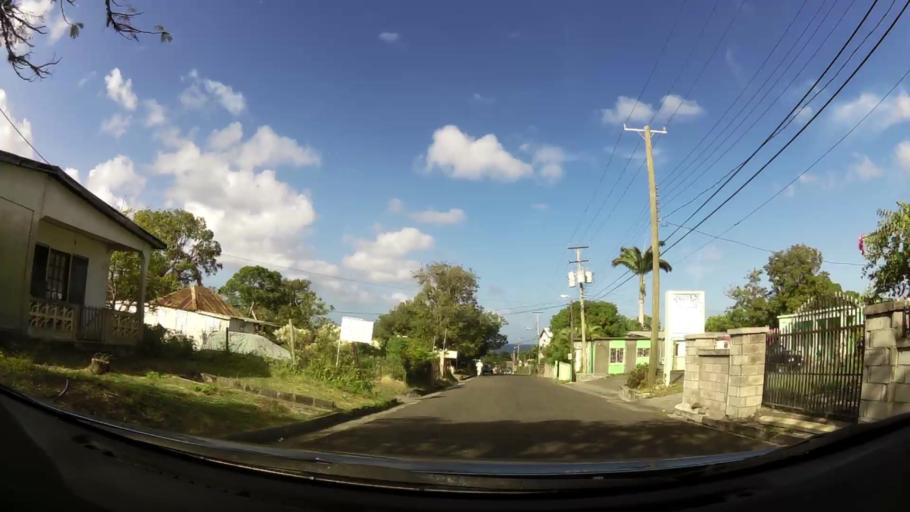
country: KN
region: Saint Paul Charlestown
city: Charlestown
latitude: 17.1373
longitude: -62.6236
